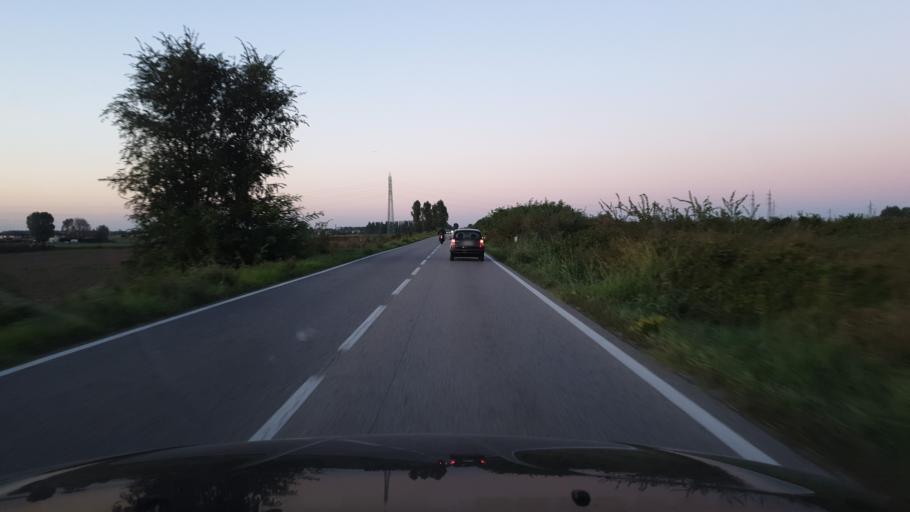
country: IT
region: Emilia-Romagna
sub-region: Provincia di Bologna
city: Minerbio
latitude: 44.6435
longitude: 11.4762
